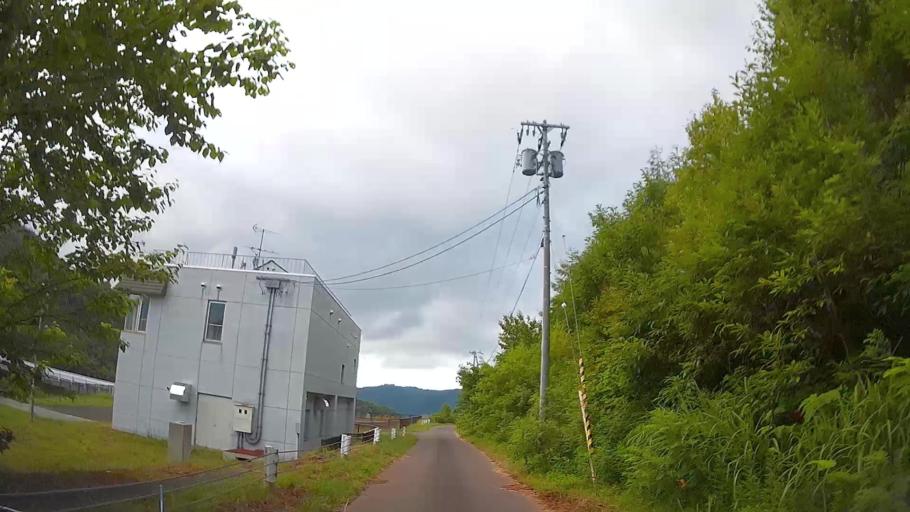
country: JP
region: Hokkaido
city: Nanae
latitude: 42.1009
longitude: 140.4526
